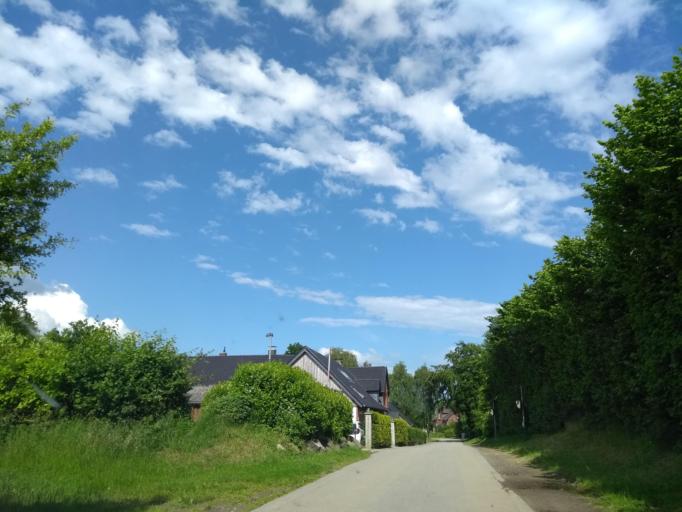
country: DE
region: Schleswig-Holstein
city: Thumby
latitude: 54.5543
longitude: 9.9384
